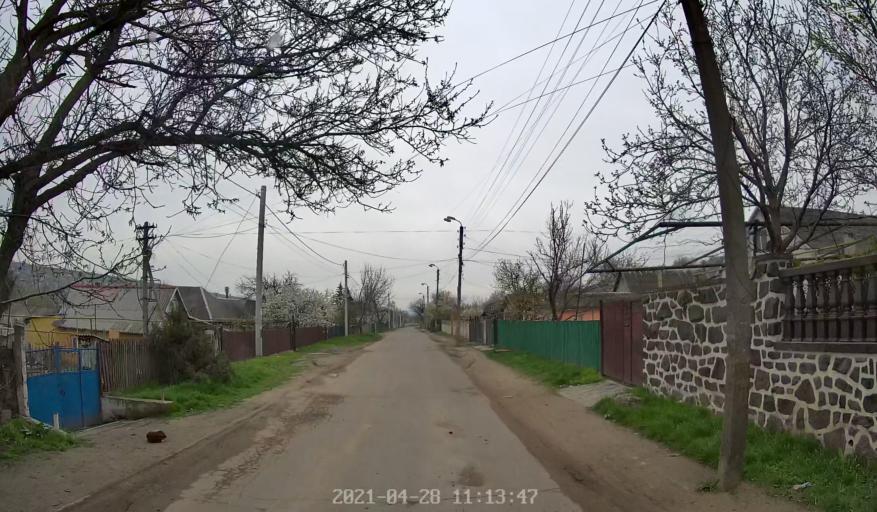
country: MD
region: Chisinau
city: Singera
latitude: 46.9831
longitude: 28.9367
